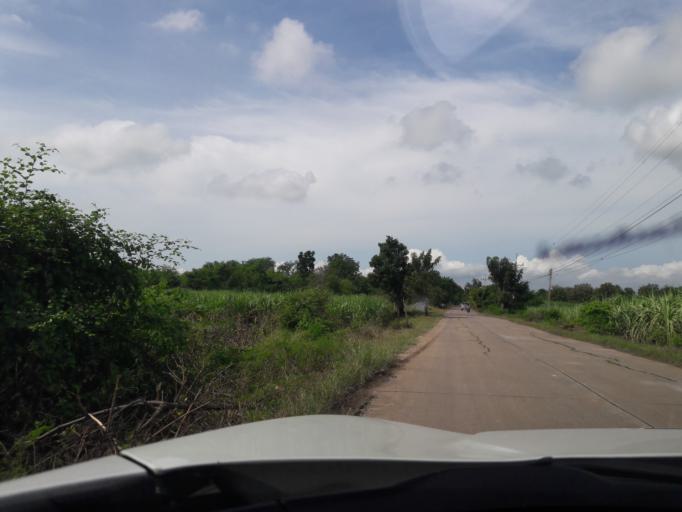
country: TH
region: Lop Buri
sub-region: Amphoe Tha Luang
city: Tha Luang
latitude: 15.0736
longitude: 101.1178
